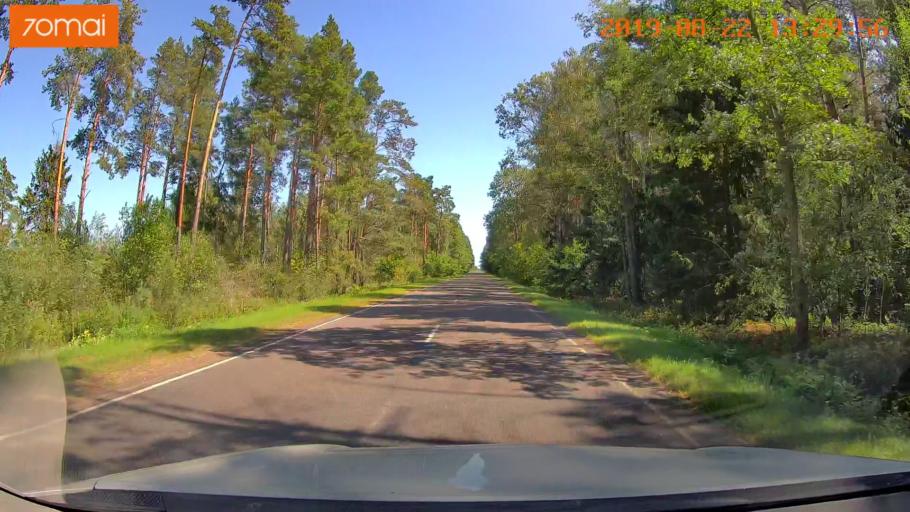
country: BY
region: Minsk
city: Staryya Darohi
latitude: 53.2173
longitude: 28.1438
